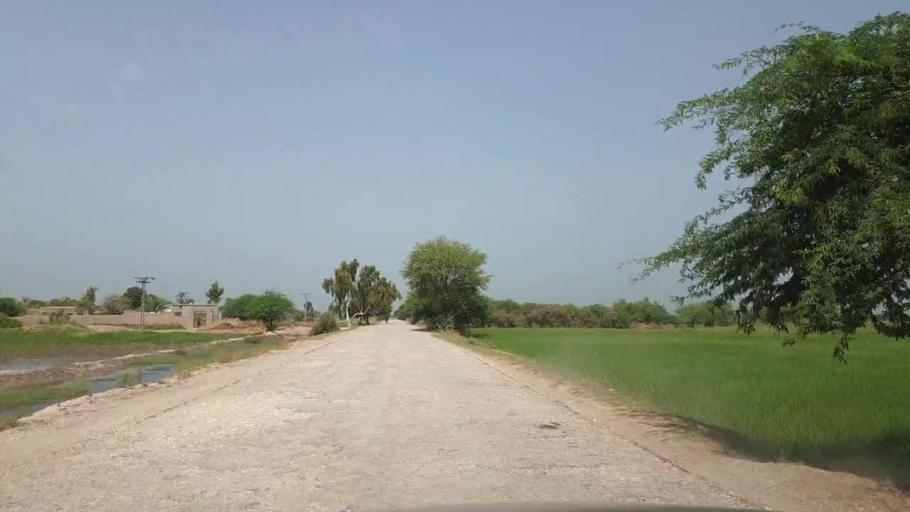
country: PK
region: Sindh
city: Garhi Yasin
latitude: 27.8569
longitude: 68.4169
